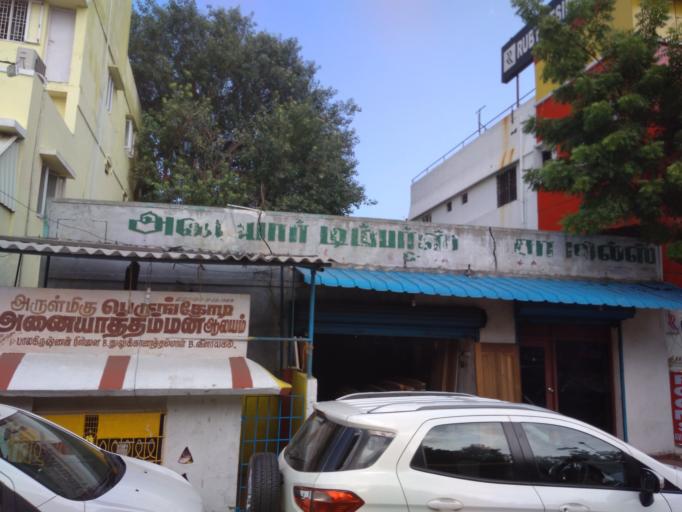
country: IN
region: Tamil Nadu
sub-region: Chennai
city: Gandhi Nagar
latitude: 12.9840
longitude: 80.2551
